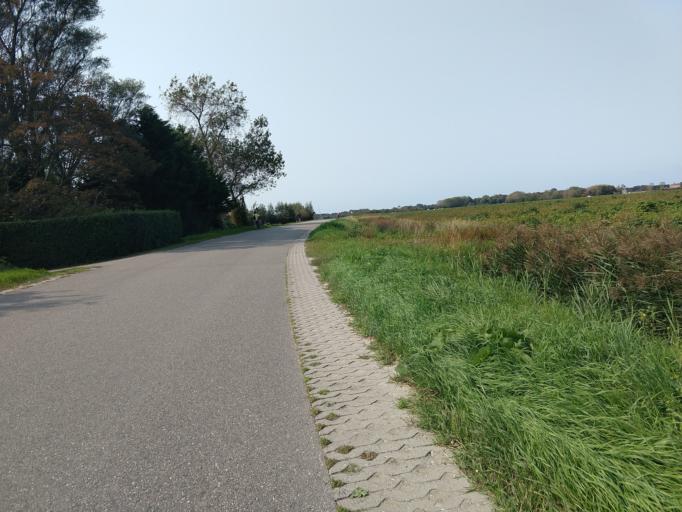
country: NL
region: Zeeland
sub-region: Schouwen-Duiveland
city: Renesse
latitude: 51.7271
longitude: 3.8026
